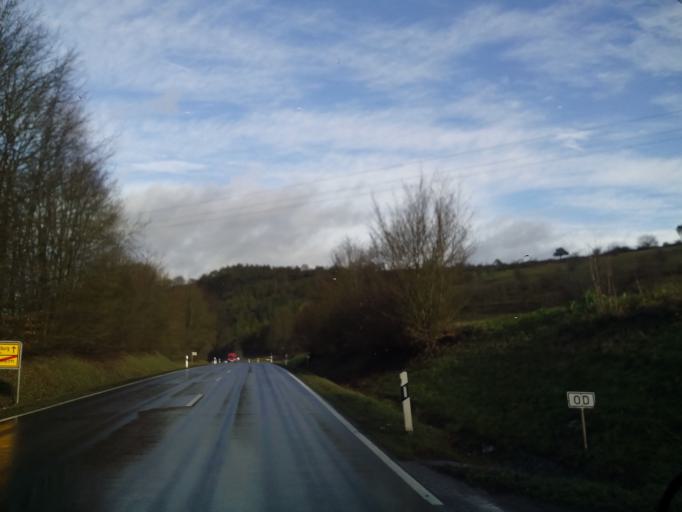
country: DE
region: Bavaria
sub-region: Regierungsbezirk Unterfranken
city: Eussenheim
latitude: 49.9918
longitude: 9.8112
